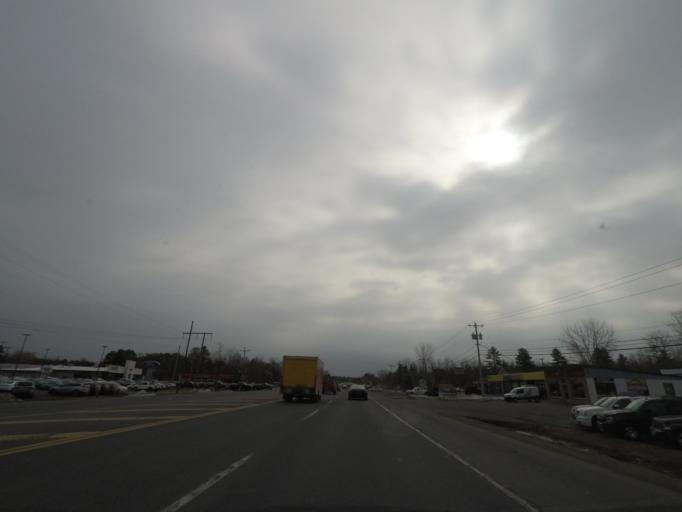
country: US
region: New York
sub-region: Warren County
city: Glens Falls
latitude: 43.3319
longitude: -73.6460
